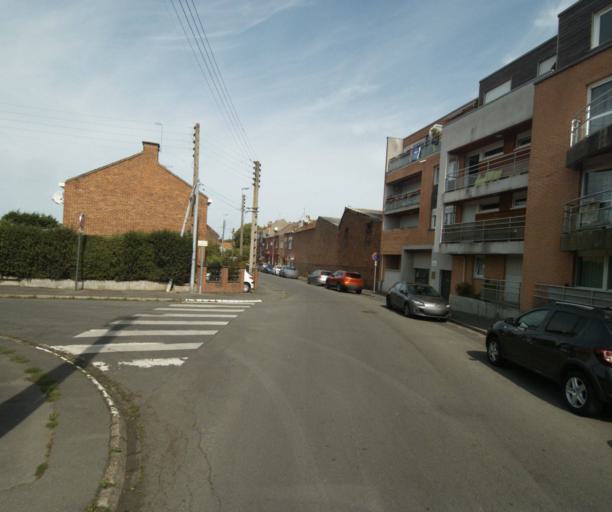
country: FR
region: Nord-Pas-de-Calais
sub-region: Departement du Nord
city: Faches-Thumesnil
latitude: 50.6051
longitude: 3.0655
